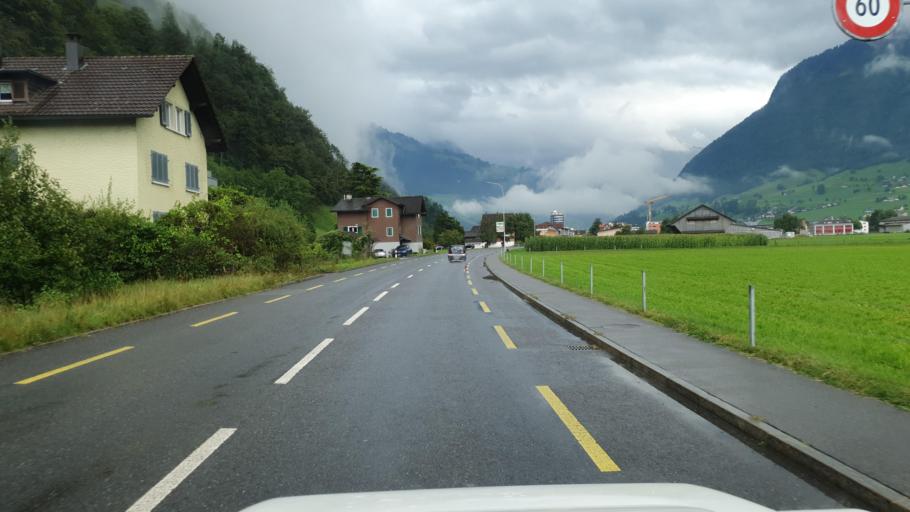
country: CH
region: Nidwalden
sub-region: Nidwalden
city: Stansstad
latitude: 46.9735
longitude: 8.3463
